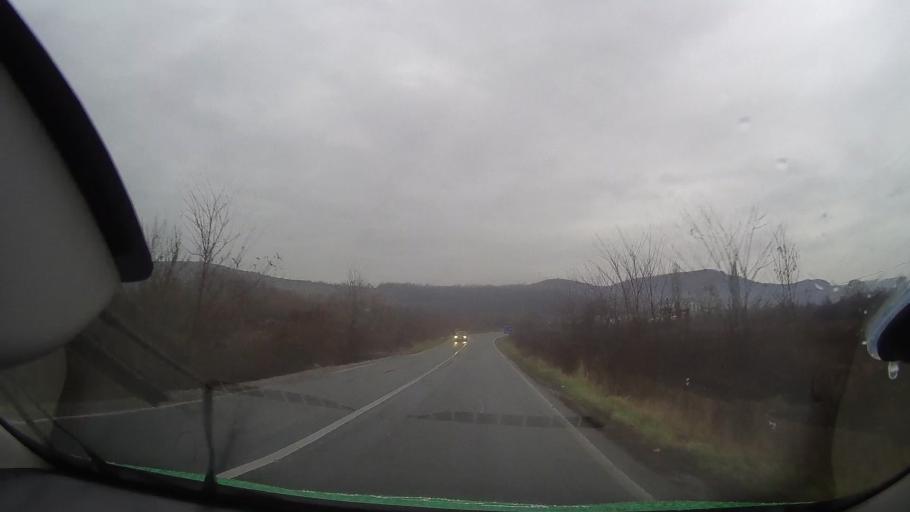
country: RO
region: Bihor
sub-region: Comuna Sambata
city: Sambata
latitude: 46.7922
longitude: 22.2040
